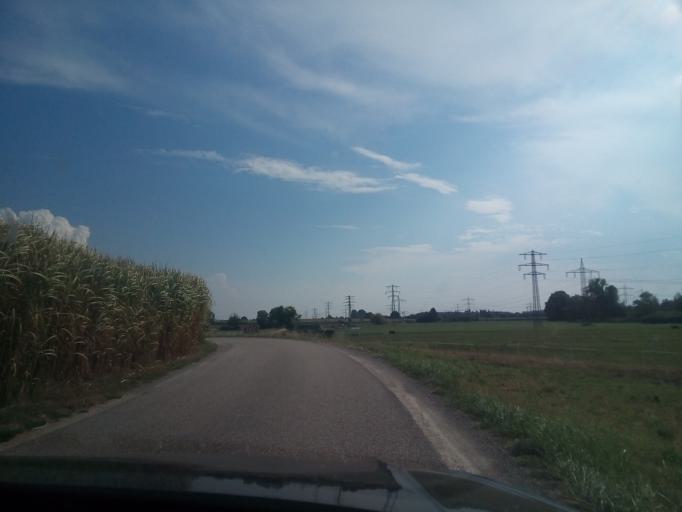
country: DE
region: Baden-Wuerttemberg
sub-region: Karlsruhe Region
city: Sinzheim
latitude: 48.7713
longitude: 8.1524
